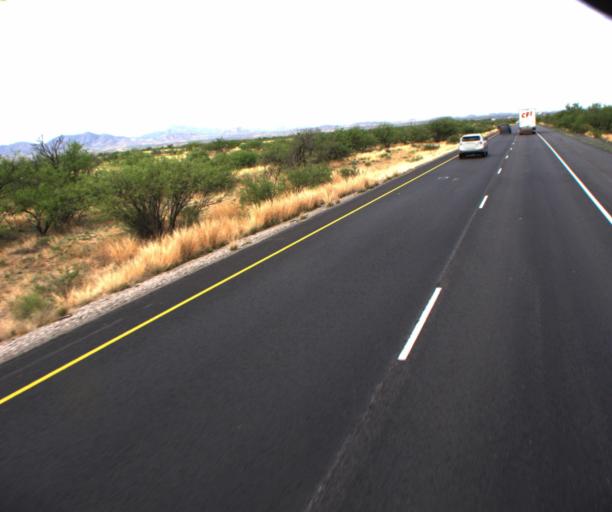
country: US
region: Arizona
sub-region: Cochise County
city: Mescal
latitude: 31.9741
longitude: -110.4956
